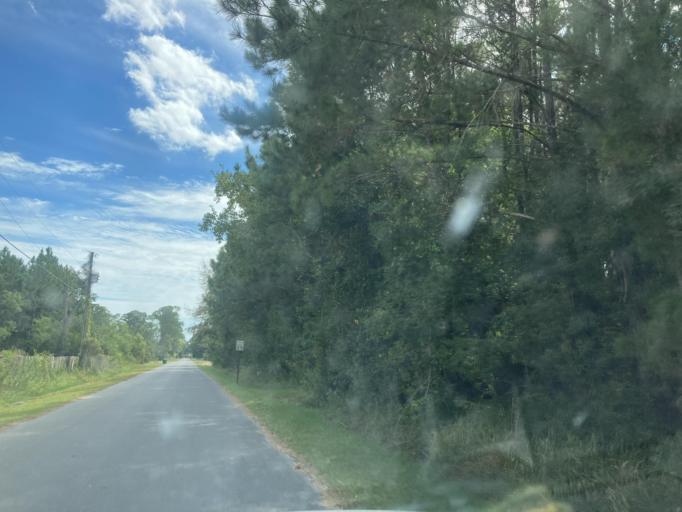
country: US
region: Mississippi
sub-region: Jackson County
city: Saint Martin
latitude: 30.4412
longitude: -88.8739
